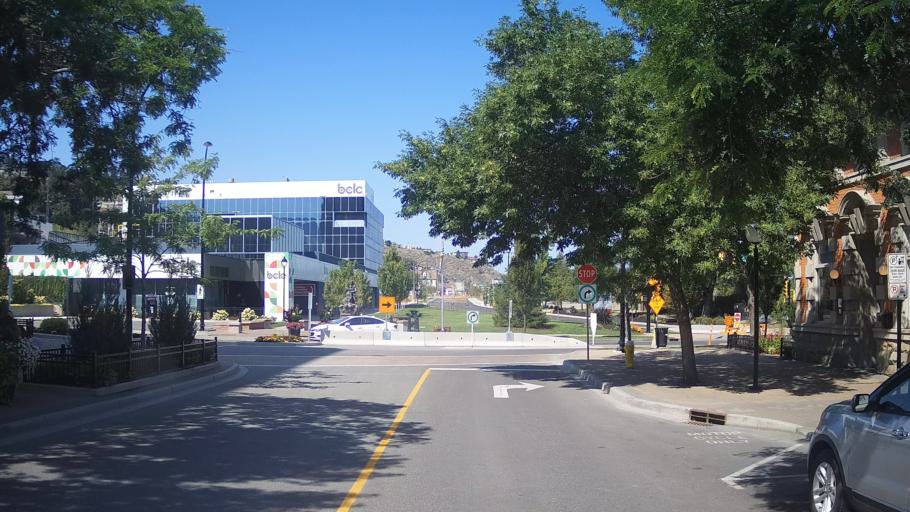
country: CA
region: British Columbia
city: Kamloops
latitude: 50.6763
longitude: -120.3384
